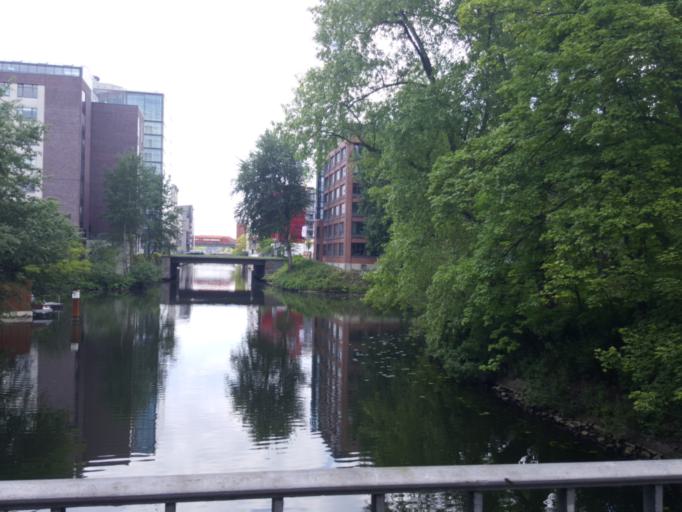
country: DE
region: Hamburg
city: Hammerbrook
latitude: 53.5491
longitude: 10.0302
